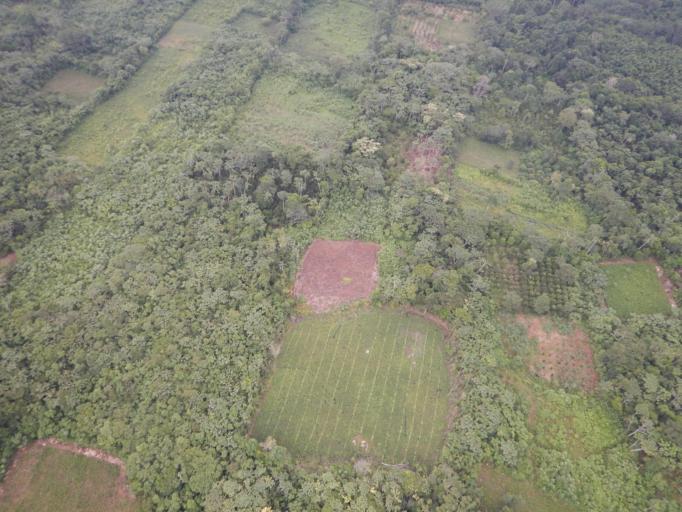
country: BO
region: Cochabamba
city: Chimore
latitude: -17.2705
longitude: -64.6121
